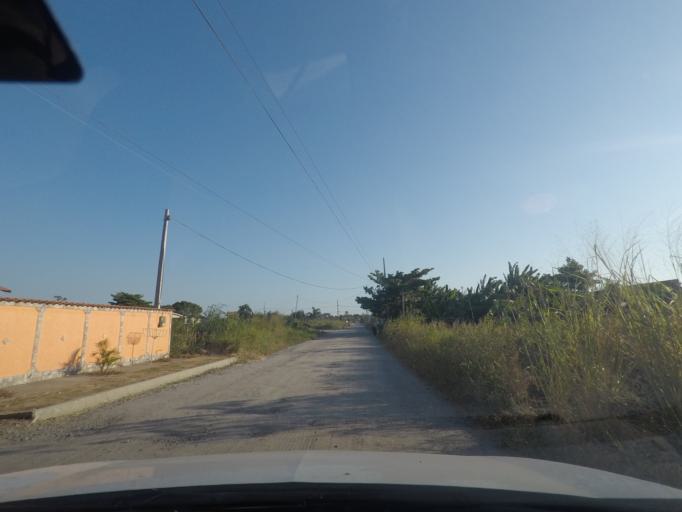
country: BR
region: Rio de Janeiro
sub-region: Marica
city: Marica
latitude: -22.9633
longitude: -42.9325
